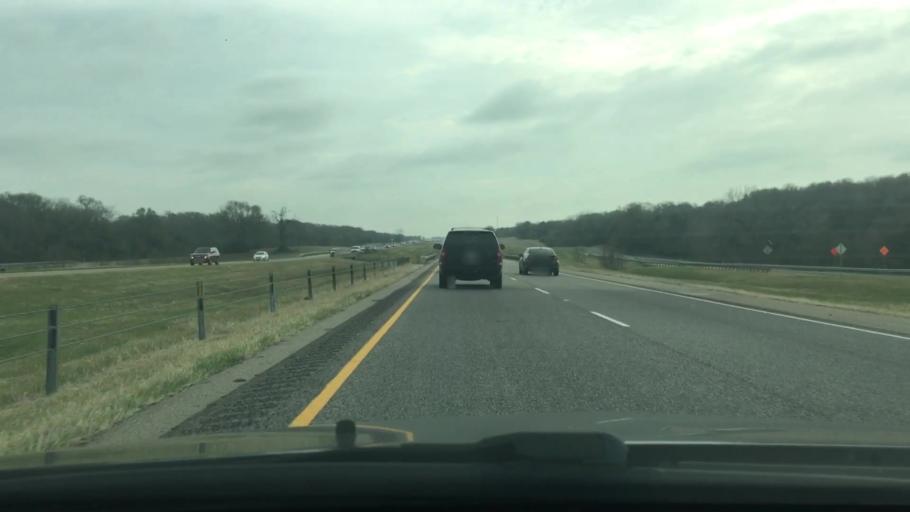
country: US
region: Texas
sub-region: Freestone County
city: Fairfield
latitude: 31.6285
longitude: -96.1578
